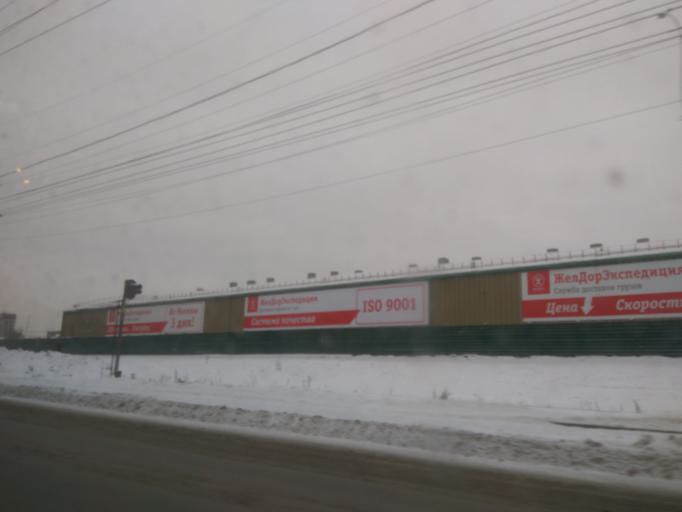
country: RU
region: Novosibirsk
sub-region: Novosibirskiy Rayon
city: Novosibirsk
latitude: 55.0422
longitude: 82.8836
